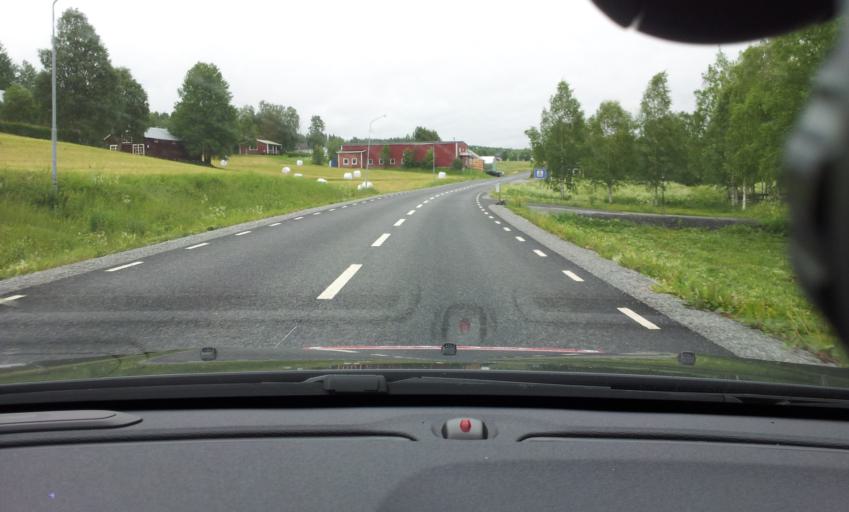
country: SE
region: Jaemtland
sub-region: OEstersunds Kommun
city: Lit
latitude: 63.7430
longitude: 14.8394
